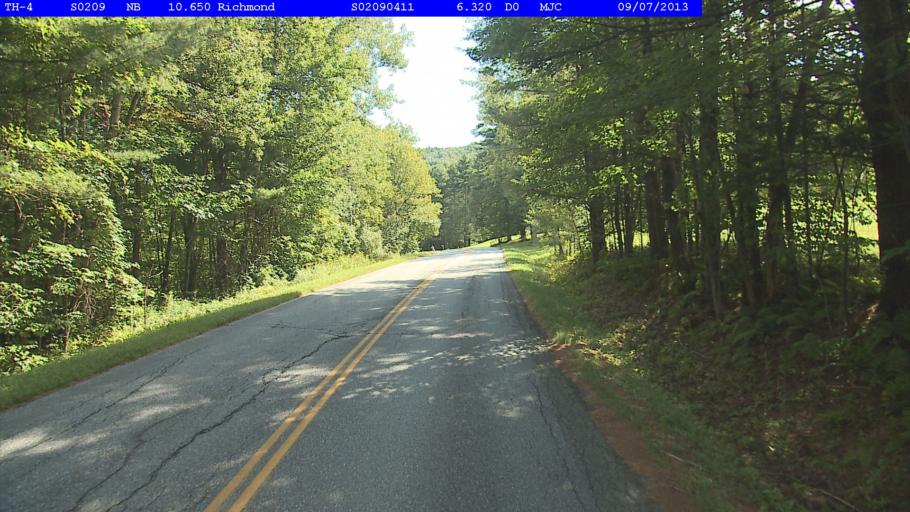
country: US
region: Vermont
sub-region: Chittenden County
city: Williston
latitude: 44.4182
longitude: -72.9839
